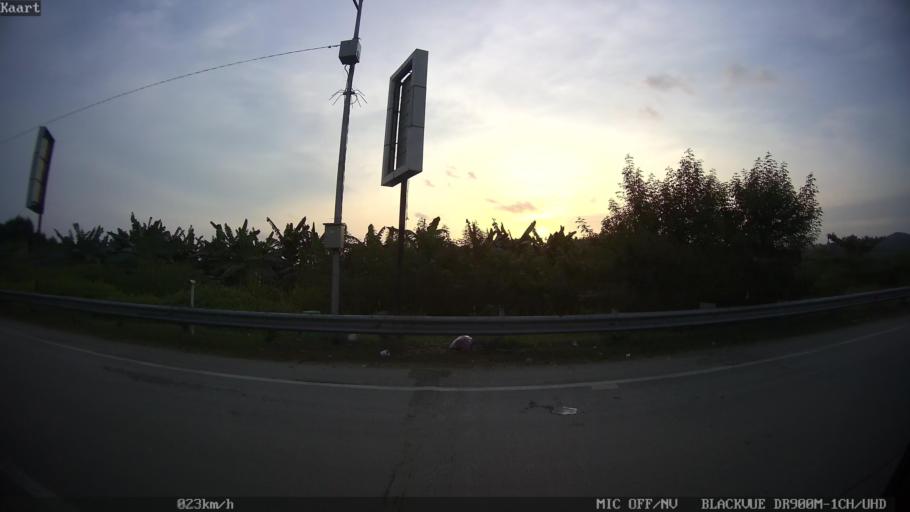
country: ID
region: Lampung
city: Penengahan
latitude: -5.8722
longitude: 105.7500
